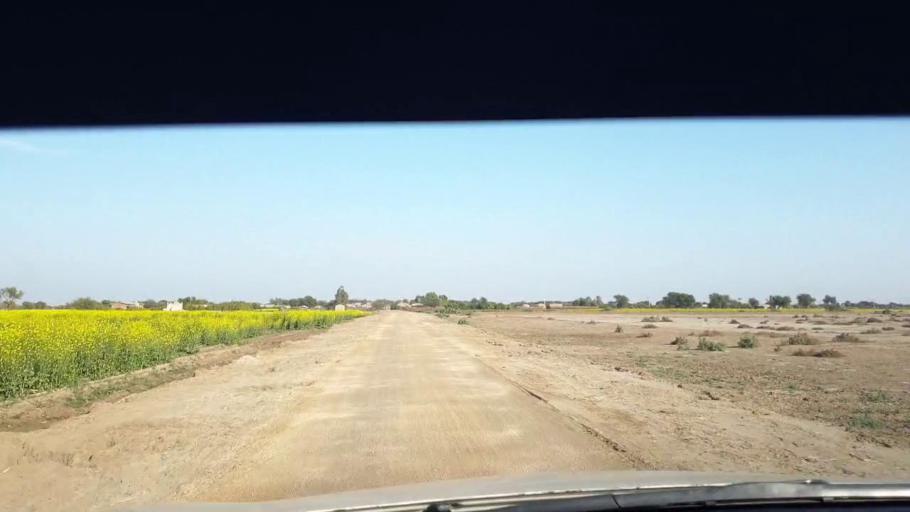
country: PK
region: Sindh
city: Berani
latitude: 25.7898
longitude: 68.9298
